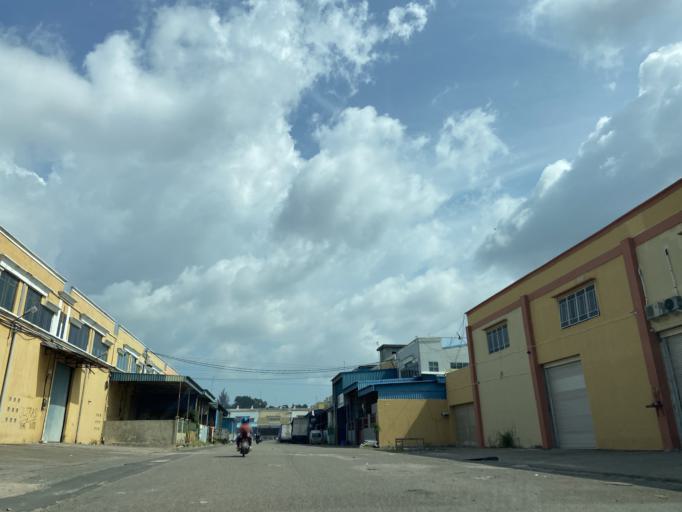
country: SG
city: Singapore
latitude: 1.1341
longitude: 104.0301
